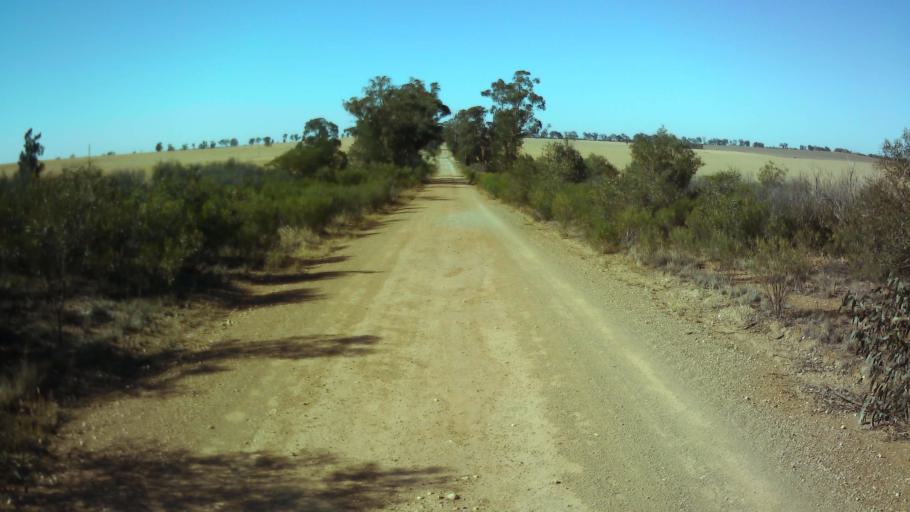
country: AU
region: New South Wales
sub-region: Weddin
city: Grenfell
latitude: -33.8835
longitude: 147.8819
